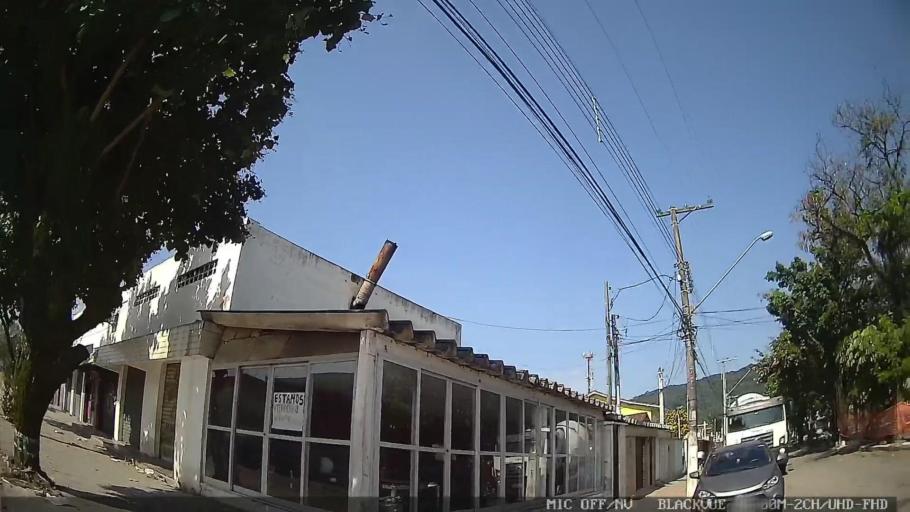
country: BR
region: Sao Paulo
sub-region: Guaruja
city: Guaruja
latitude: -23.9847
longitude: -46.2697
